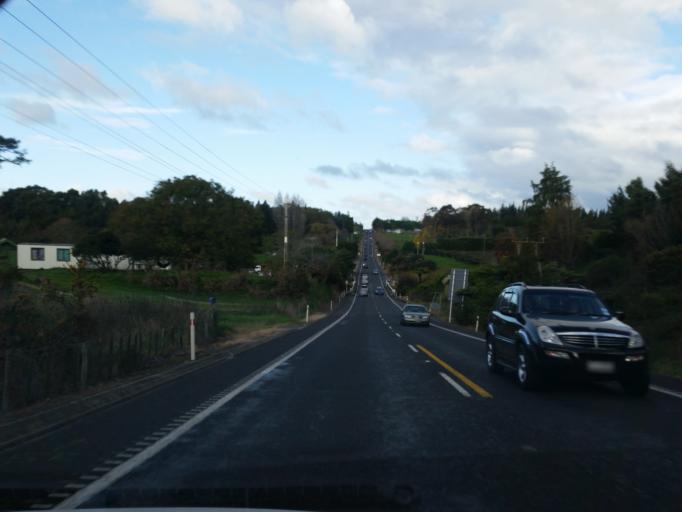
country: NZ
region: Bay of Plenty
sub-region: Western Bay of Plenty District
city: Katikati
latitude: -37.6574
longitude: 176.0016
